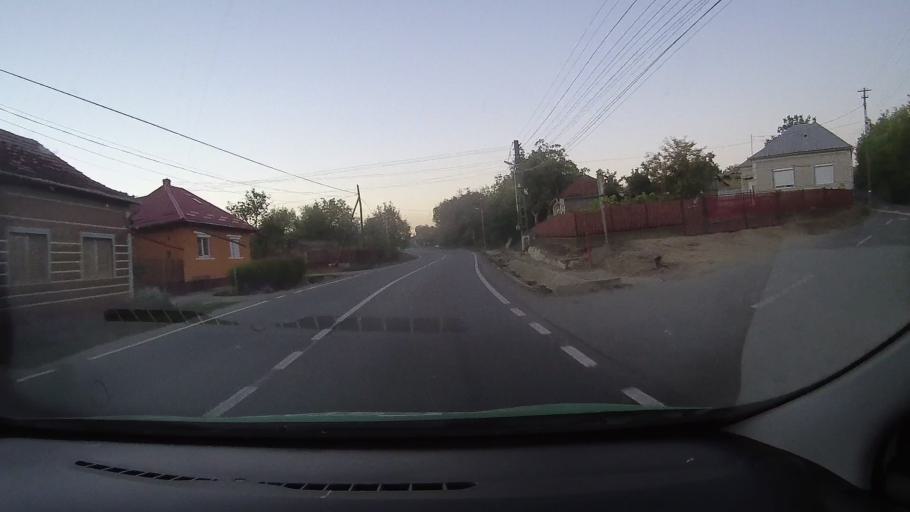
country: RO
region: Bihor
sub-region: Comuna Tarcea
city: Tarcea
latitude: 47.4605
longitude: 22.1694
